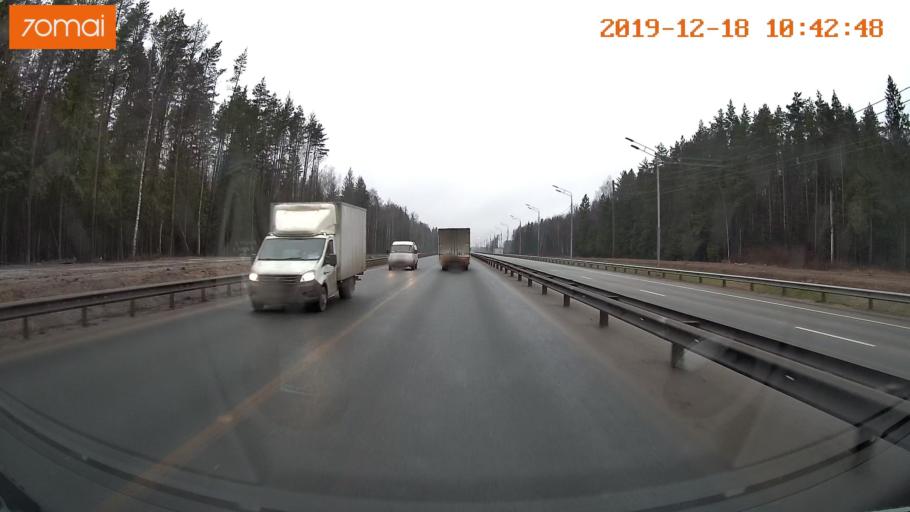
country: RU
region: Moskovskaya
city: Aprelevka
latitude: 55.4643
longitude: 37.0919
